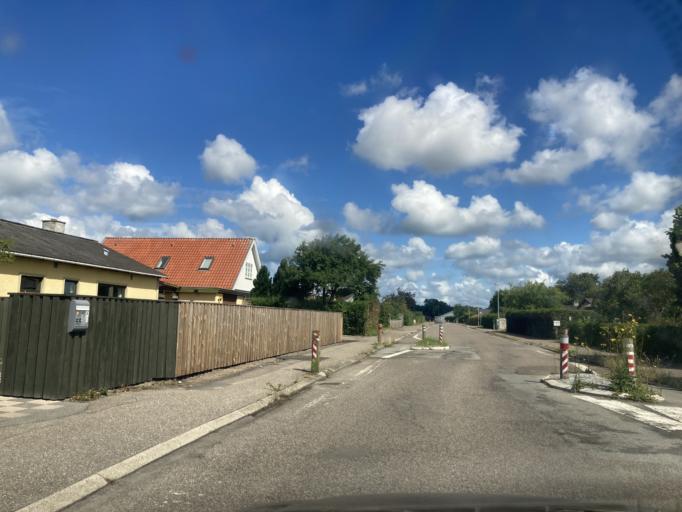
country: DK
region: Capital Region
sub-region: Halsnaes Kommune
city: Frederiksvaerk
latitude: 55.9889
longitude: 12.0100
